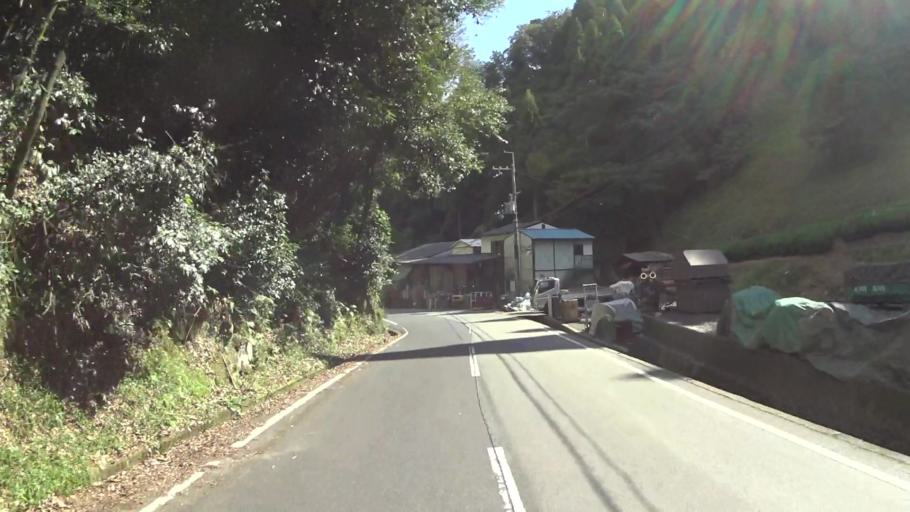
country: JP
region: Kyoto
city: Uji
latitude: 34.9103
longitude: 135.8624
